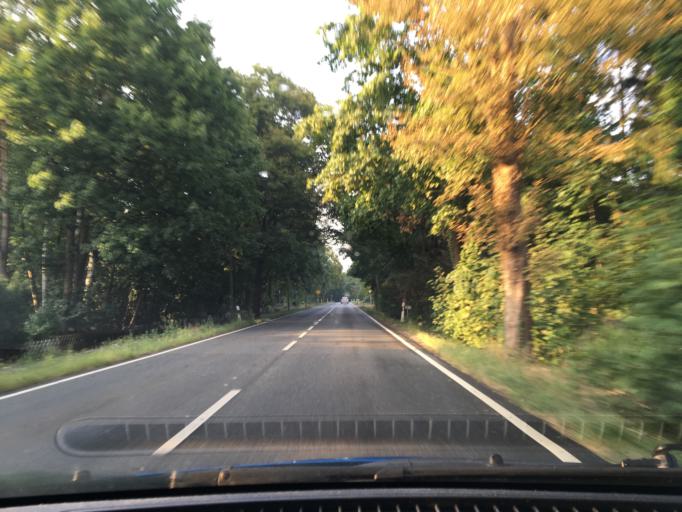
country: DE
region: Lower Saxony
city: Celle
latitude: 52.6591
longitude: 10.0668
